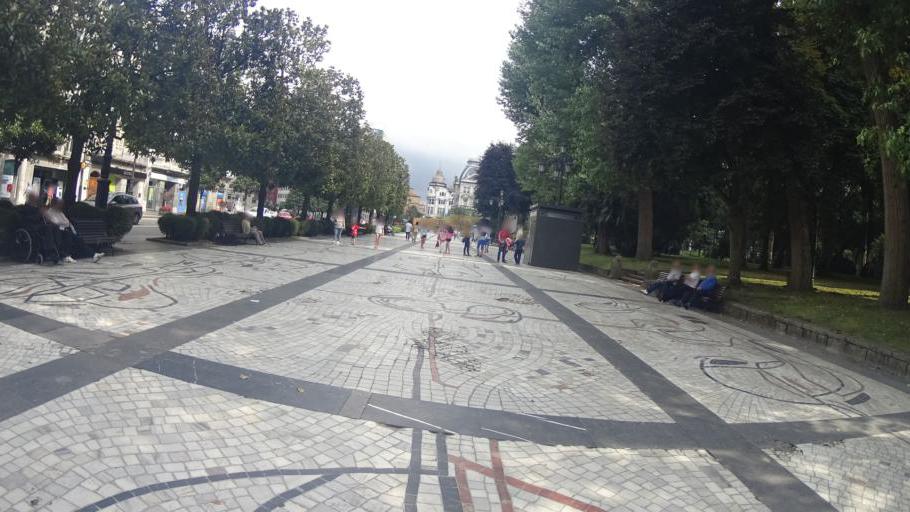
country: ES
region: Asturias
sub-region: Province of Asturias
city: Oviedo
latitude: 43.3626
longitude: -5.8494
